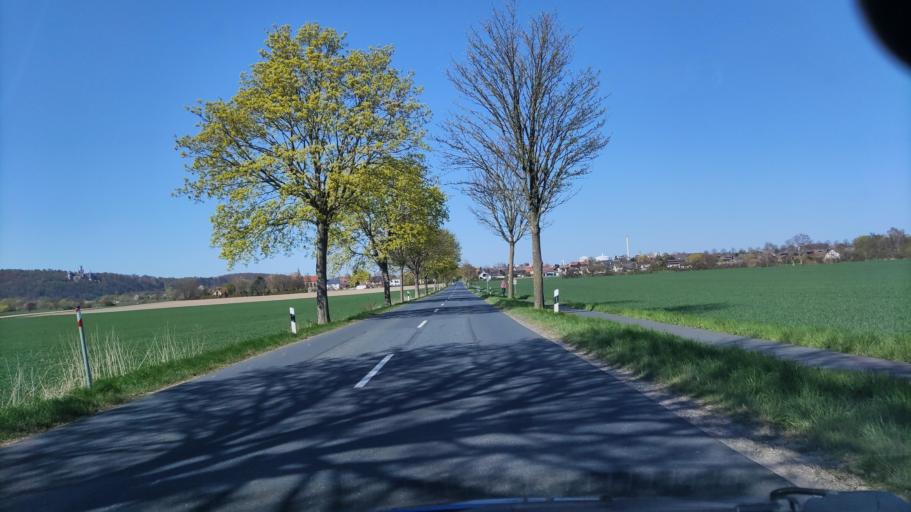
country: DE
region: Lower Saxony
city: Nordstemmen
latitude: 52.1510
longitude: 9.7762
